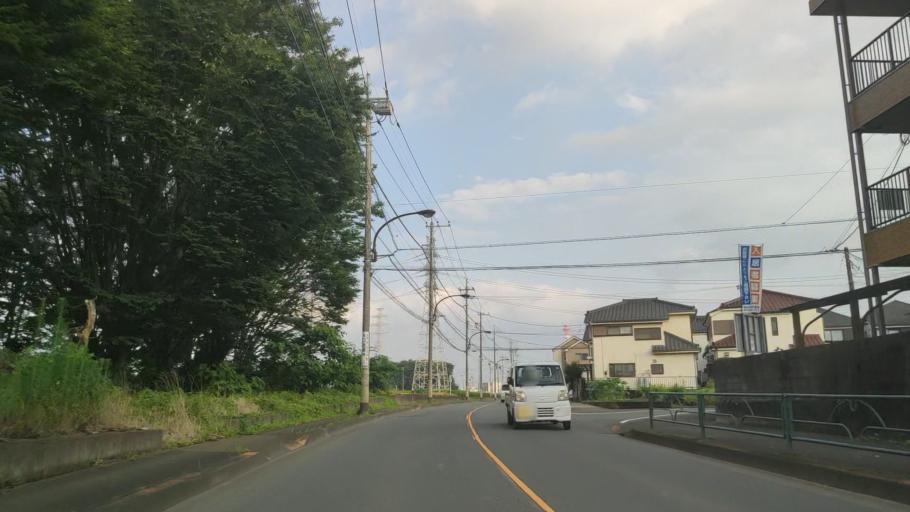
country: JP
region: Saitama
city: Hanno
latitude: 35.8010
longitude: 139.3113
